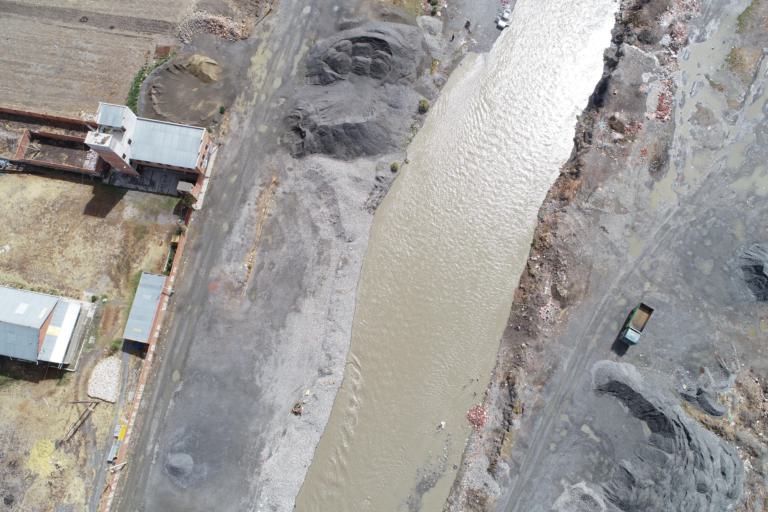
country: BO
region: La Paz
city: Achacachi
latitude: -16.0385
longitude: -68.6884
